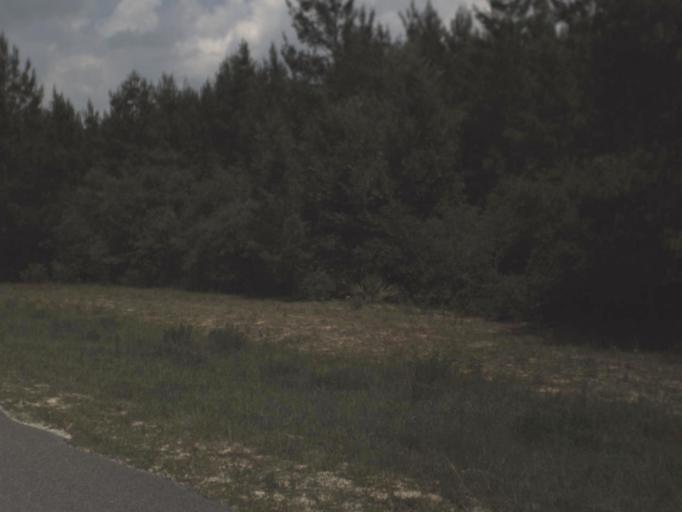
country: US
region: Florida
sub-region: Putnam County
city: Crescent City
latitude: 29.4343
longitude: -81.7376
